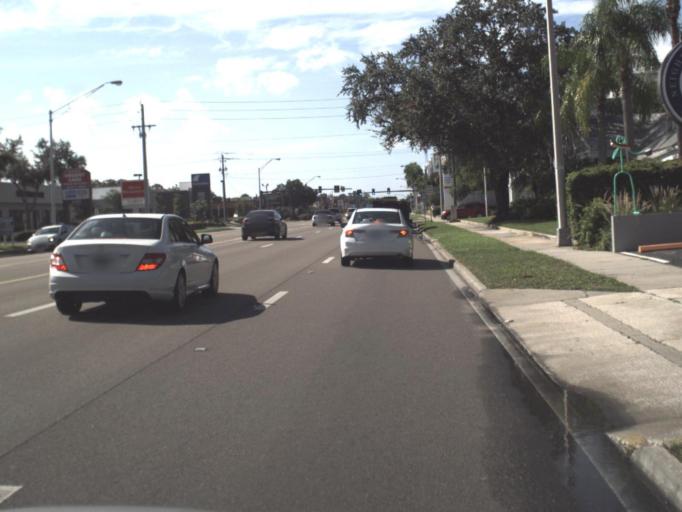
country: US
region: Florida
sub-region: Sarasota County
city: Sarasota
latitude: 27.3210
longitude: -82.5298
